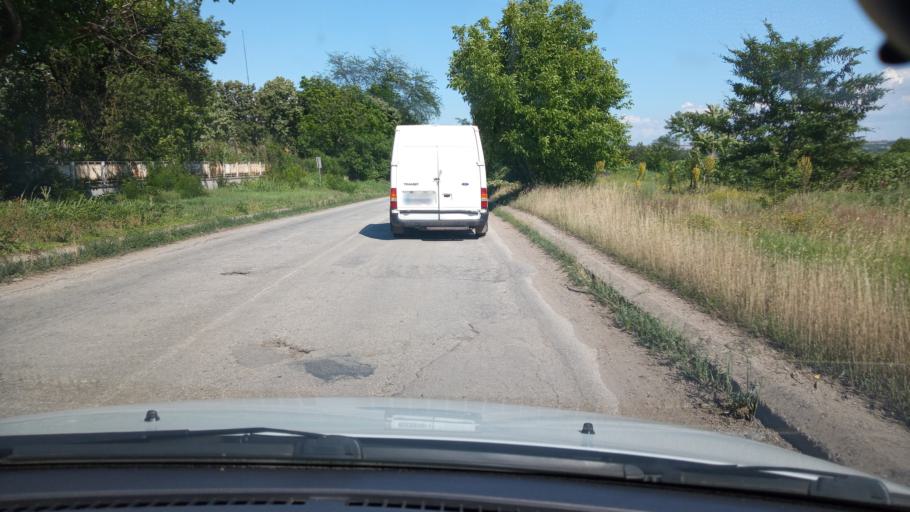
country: BG
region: Pleven
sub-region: Obshtina Dolna Mitropoliya
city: Dolna Mitropoliya
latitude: 43.4626
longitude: 24.5373
